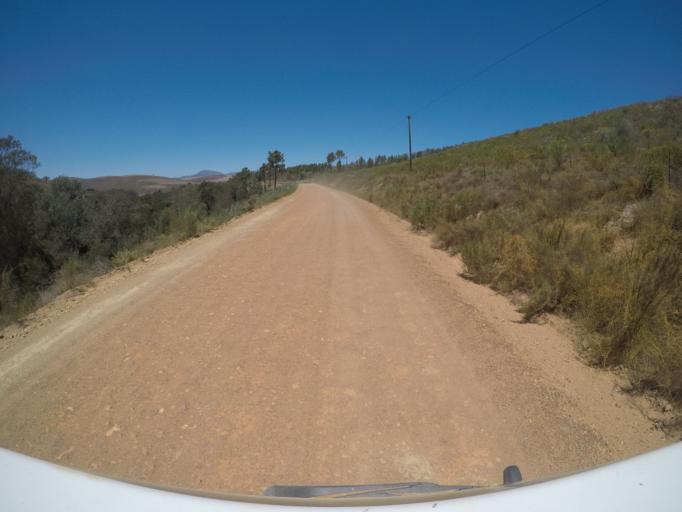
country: ZA
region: Western Cape
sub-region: Overberg District Municipality
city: Caledon
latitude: -34.1829
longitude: 19.2227
